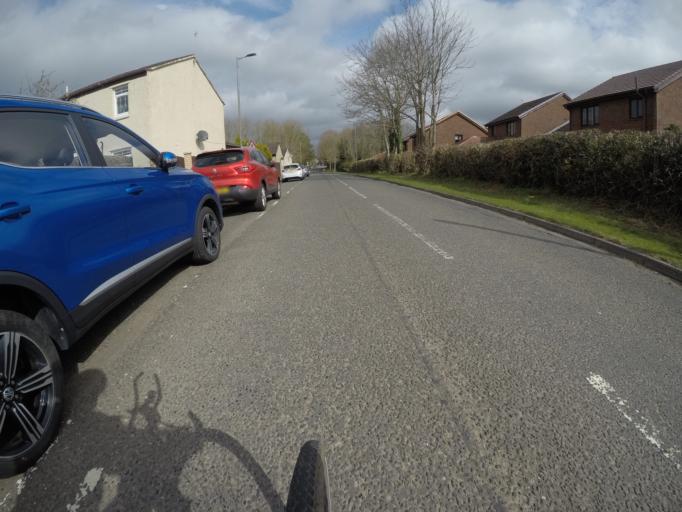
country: GB
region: Scotland
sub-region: North Ayrshire
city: Irvine
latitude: 55.6295
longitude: -4.6372
